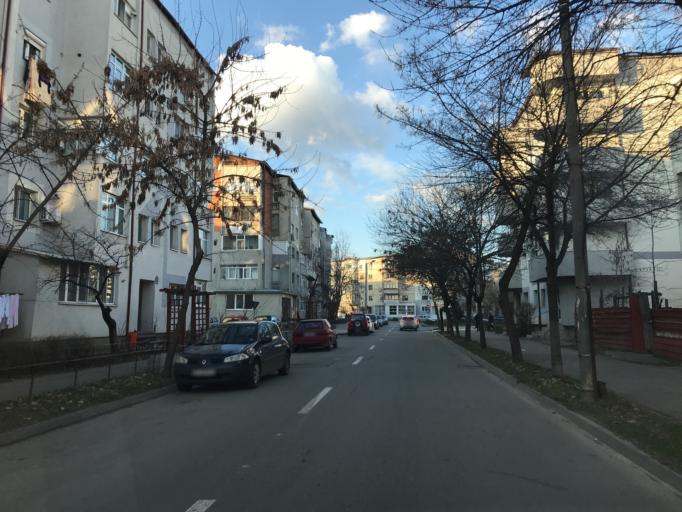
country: RO
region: Olt
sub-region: Municipiul Slatina
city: Slatina
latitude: 44.4222
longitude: 24.3816
